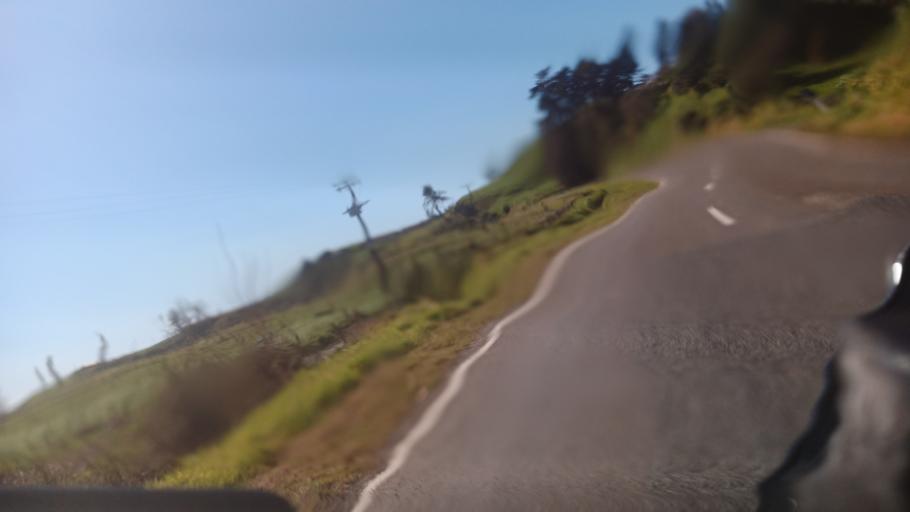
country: NZ
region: Bay of Plenty
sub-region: Opotiki District
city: Opotiki
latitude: -38.0039
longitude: 177.3962
